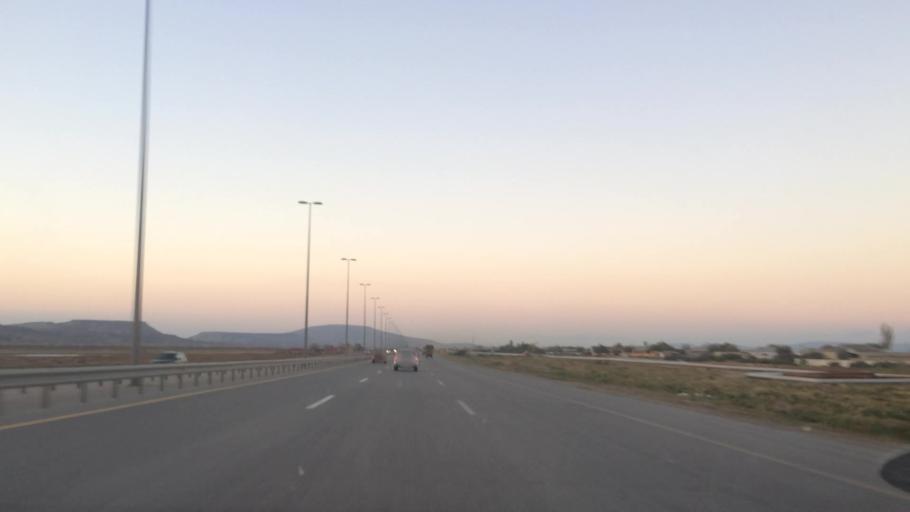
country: AZ
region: Baki
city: Qobustan
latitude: 40.0126
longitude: 49.4270
